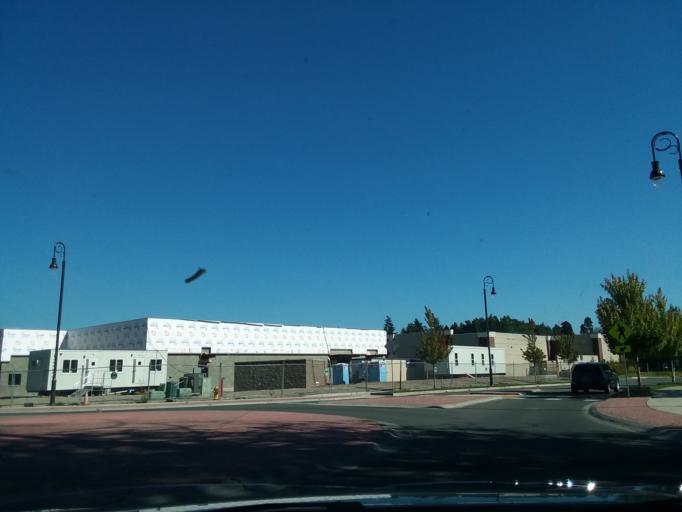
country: US
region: Washington
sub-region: Snohomish County
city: Smokey Point
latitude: 48.1537
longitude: -122.1995
